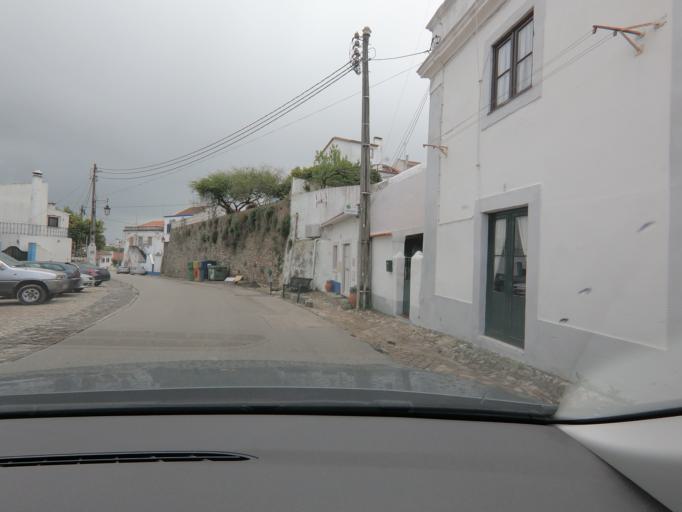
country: PT
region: Lisbon
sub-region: Alenquer
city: Alenquer
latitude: 39.0545
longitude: -9.0109
